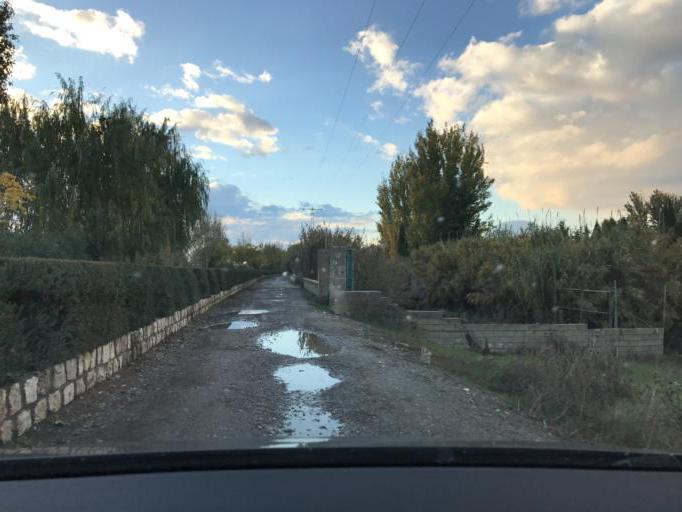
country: ES
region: Andalusia
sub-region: Provincia de Granada
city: Armilla
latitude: 37.1619
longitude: -3.6231
